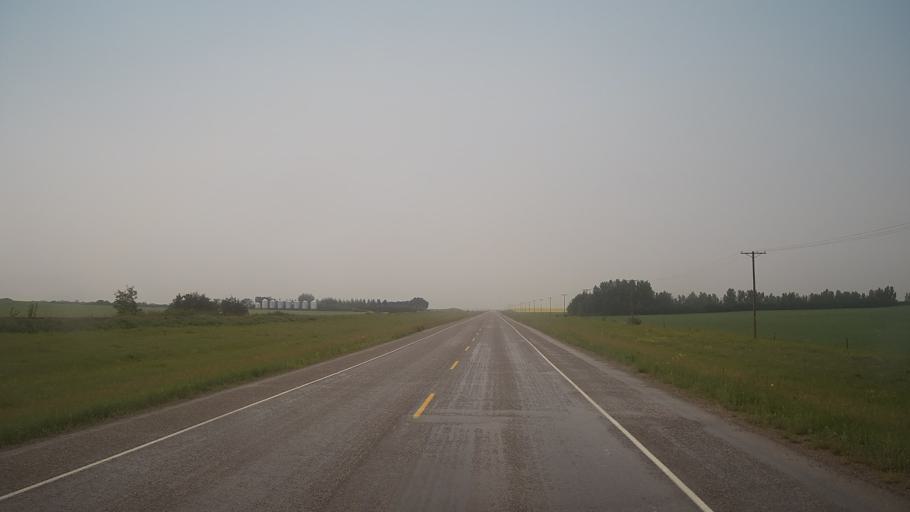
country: CA
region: Saskatchewan
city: Biggar
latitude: 52.1361
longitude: -108.1696
